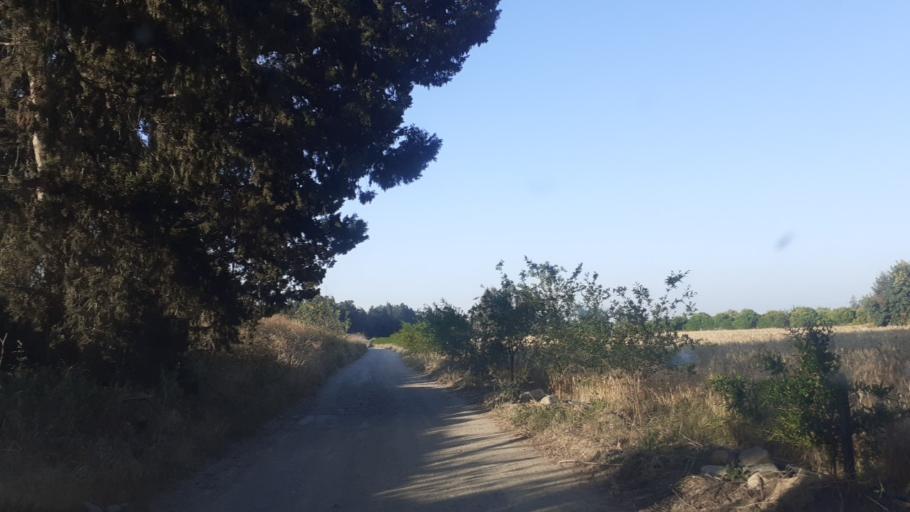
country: CY
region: Limassol
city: Ypsonas
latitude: 34.6609
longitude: 32.9800
